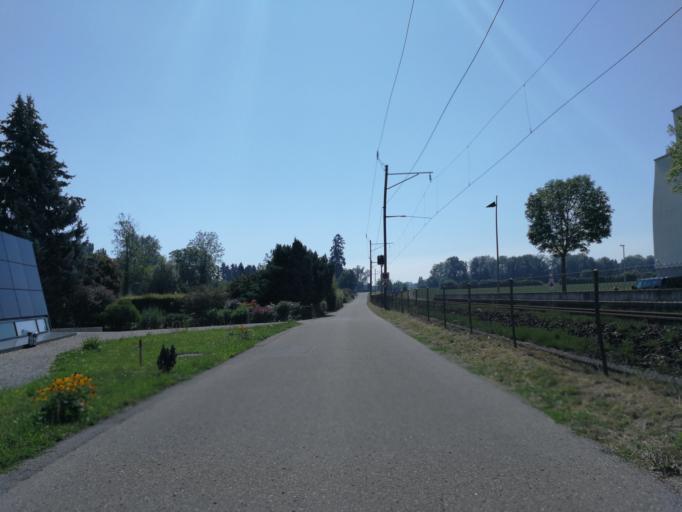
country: CH
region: Thurgau
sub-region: Kreuzlingen District
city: Bottighofen
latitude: 47.6407
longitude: 9.2134
